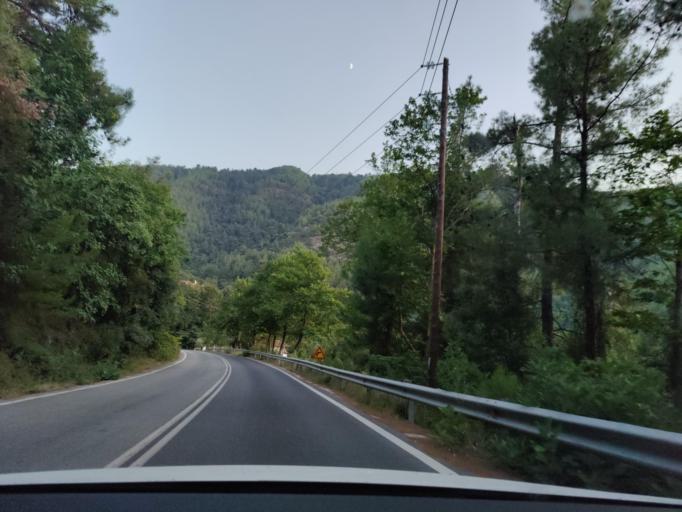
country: GR
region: East Macedonia and Thrace
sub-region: Nomos Kavalas
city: Potamia
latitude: 40.7074
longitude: 24.7633
